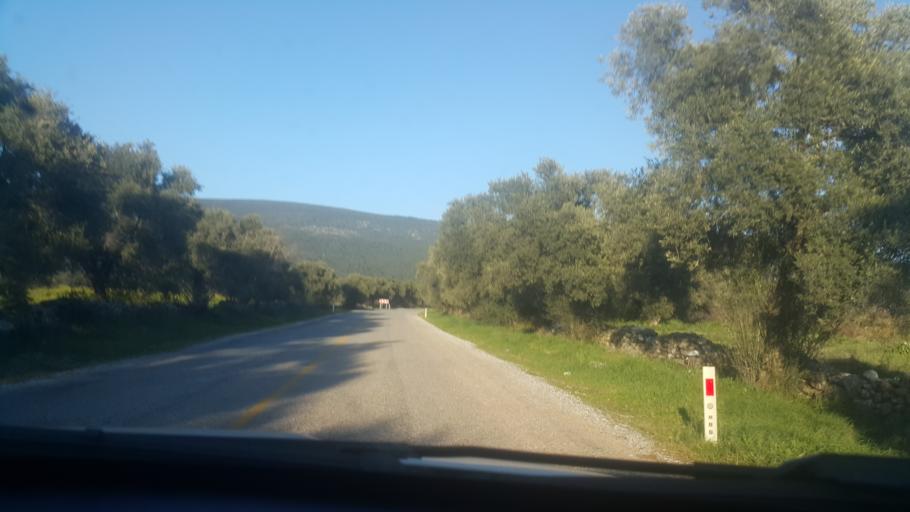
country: TR
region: Mugla
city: Kiulukioi
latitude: 37.2981
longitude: 27.5998
